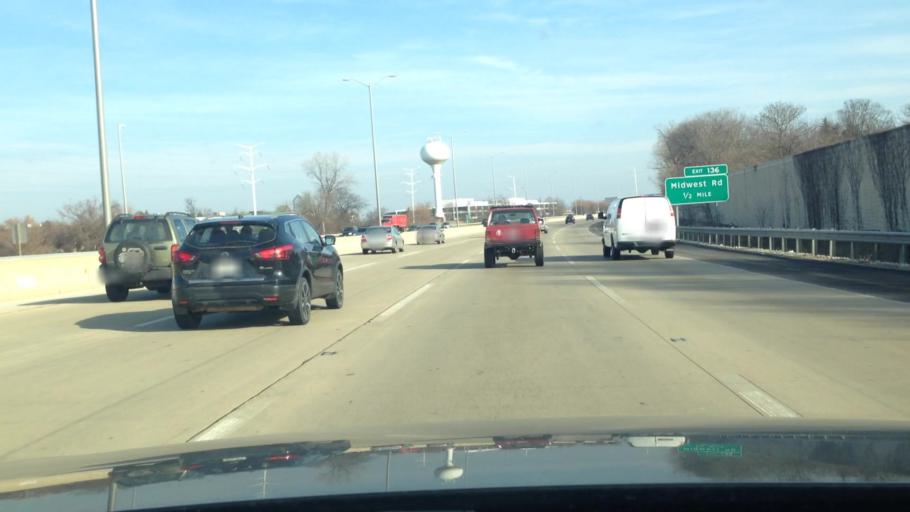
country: US
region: Illinois
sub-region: DuPage County
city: Oakbrook Terrace
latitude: 41.8428
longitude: -87.9822
